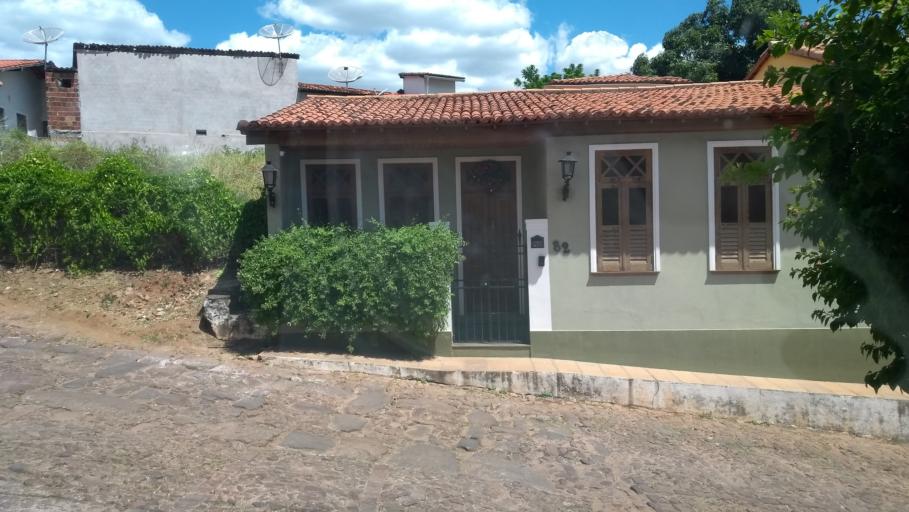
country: BR
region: Bahia
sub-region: Andarai
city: Vera Cruz
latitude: -12.5603
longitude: -41.3894
